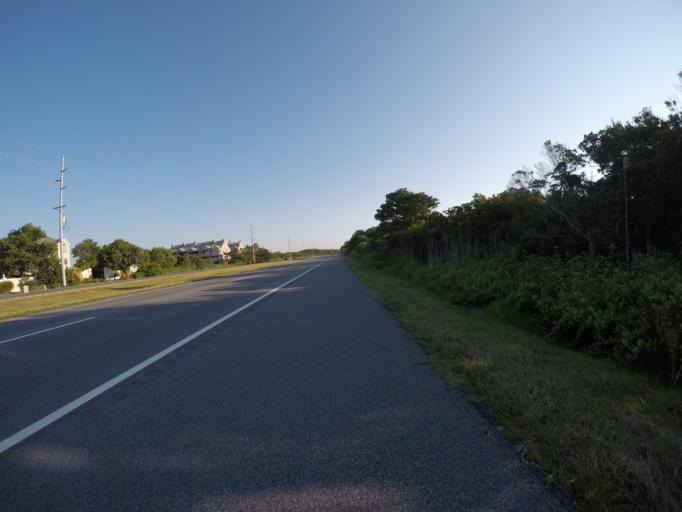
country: US
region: Delaware
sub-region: Sussex County
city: Bethany Beach
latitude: 38.4921
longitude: -75.0539
